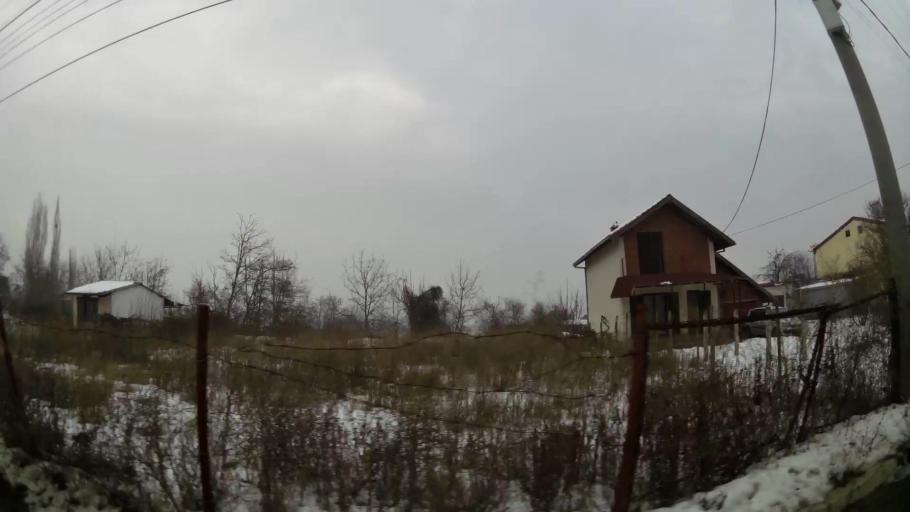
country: MK
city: Kondovo
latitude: 42.0501
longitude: 21.3467
